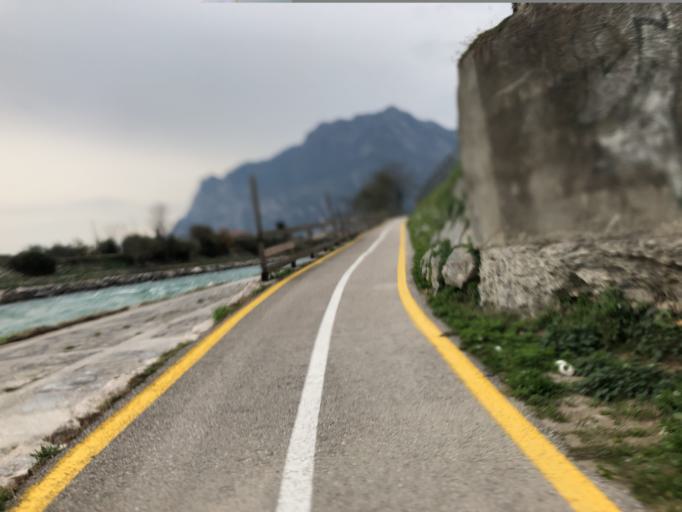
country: IT
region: Trentino-Alto Adige
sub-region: Provincia di Trento
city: Torbole sul Garda
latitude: 45.8748
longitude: 10.8730
